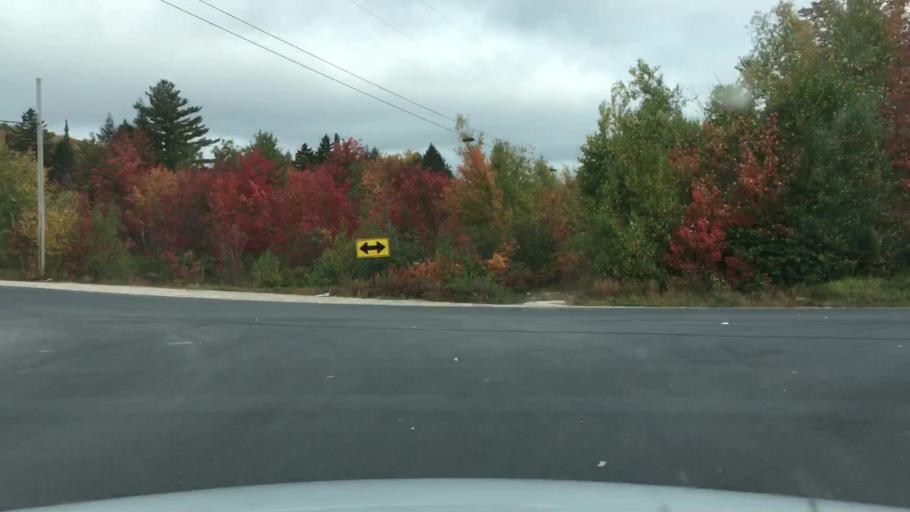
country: US
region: Maine
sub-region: Oxford County
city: Bethel
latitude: 44.3242
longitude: -70.7692
